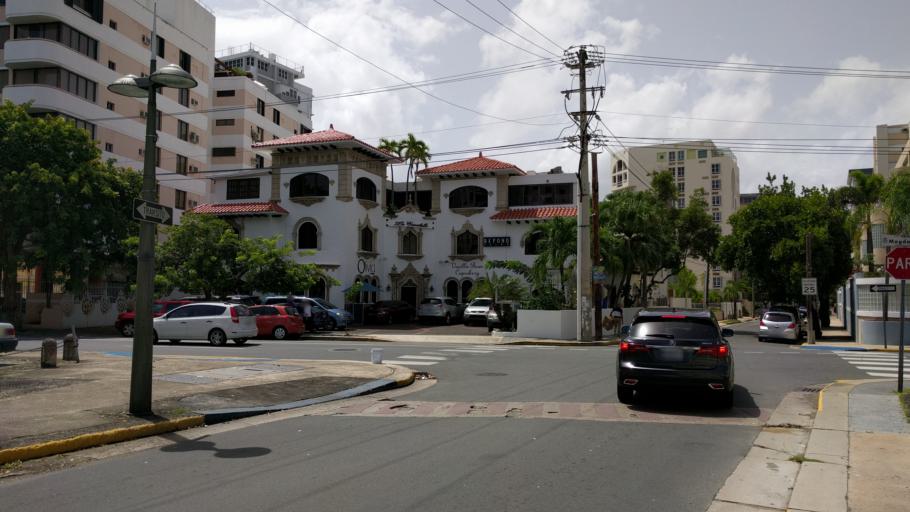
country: PR
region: San Juan
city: San Juan
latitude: 18.4547
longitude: -66.0673
